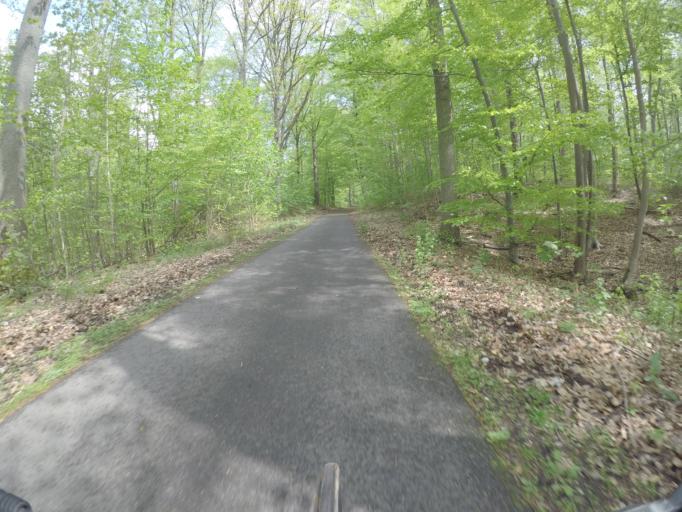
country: DE
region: Brandenburg
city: Joachimsthal
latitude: 52.9599
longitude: 13.7266
